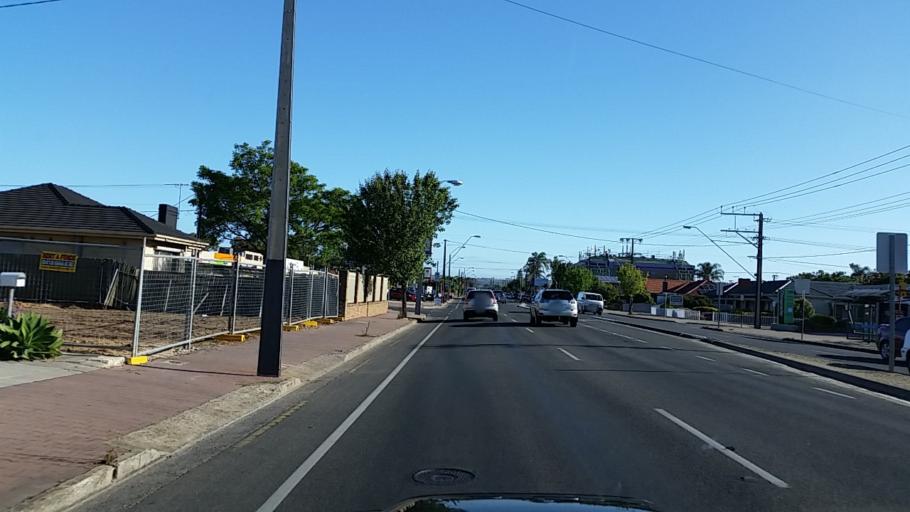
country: AU
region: South Australia
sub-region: Marion
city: South Plympton
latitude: -34.9758
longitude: 138.5557
